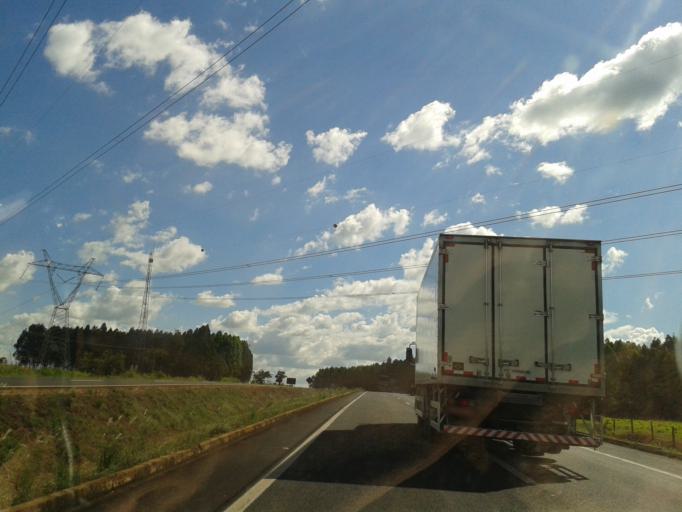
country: BR
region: Goias
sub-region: Morrinhos
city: Morrinhos
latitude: -17.7971
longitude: -49.2038
